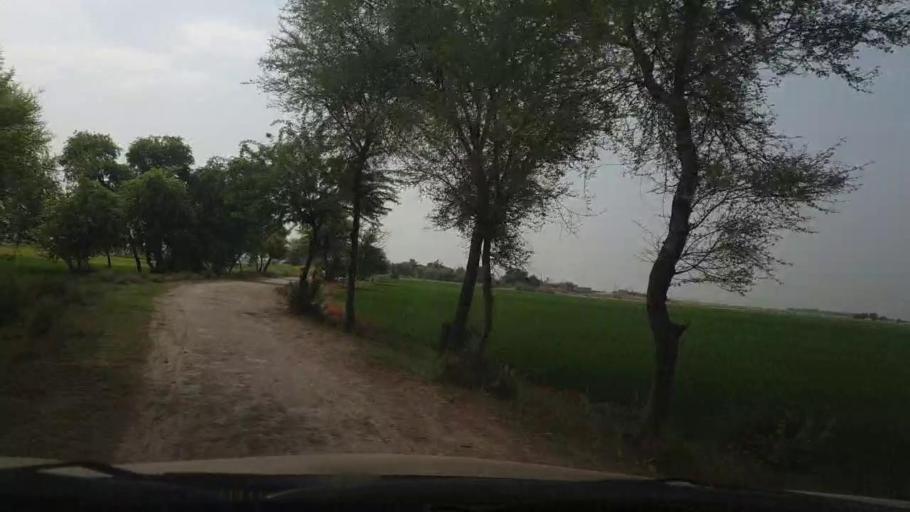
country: PK
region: Sindh
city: Larkana
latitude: 27.6838
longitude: 68.2018
